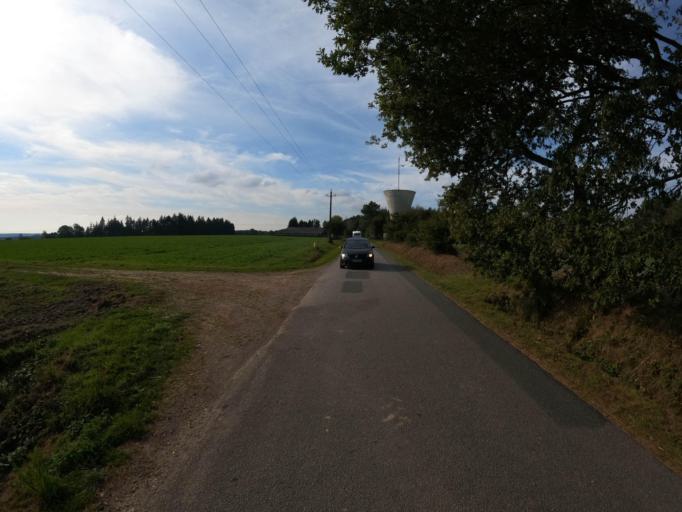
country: FR
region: Brittany
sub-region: Departement du Morbihan
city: Ploermel
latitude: 47.8801
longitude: -2.3874
